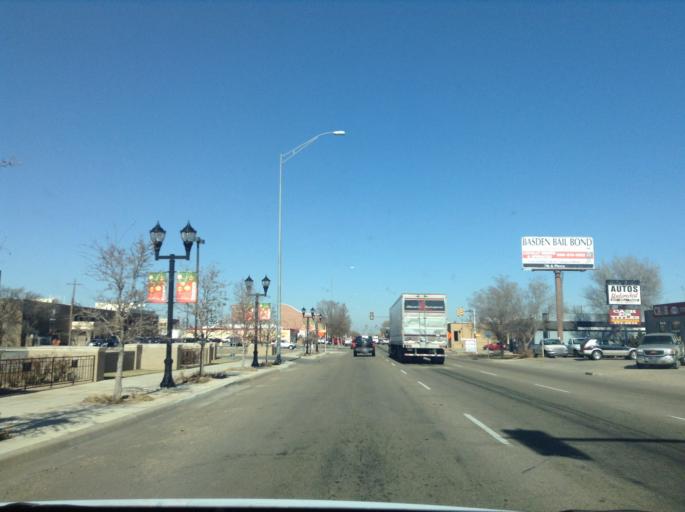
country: US
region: Texas
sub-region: Potter County
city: Amarillo
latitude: 35.2029
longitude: -101.8329
